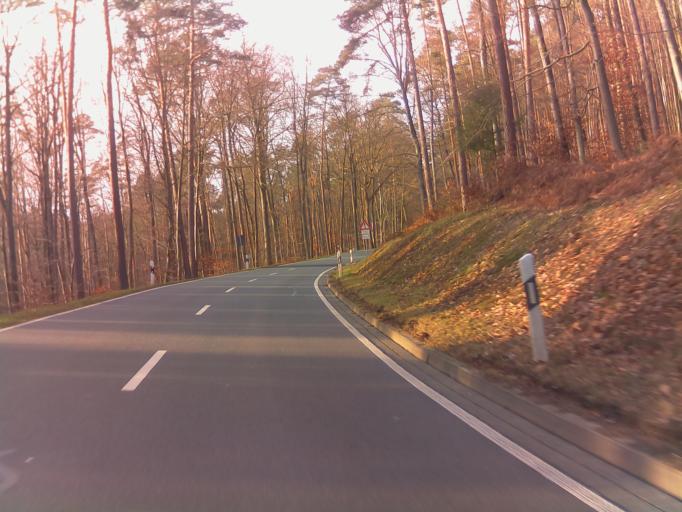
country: DE
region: Bavaria
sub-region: Regierungsbezirk Unterfranken
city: Laudenbach
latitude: 49.7460
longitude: 9.1456
